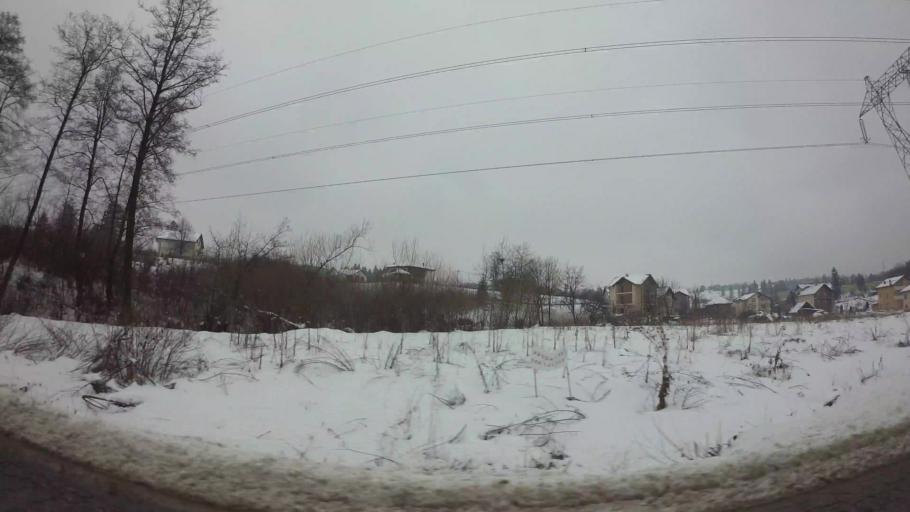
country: BA
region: Federation of Bosnia and Herzegovina
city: Hadzici
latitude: 43.8603
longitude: 18.2720
